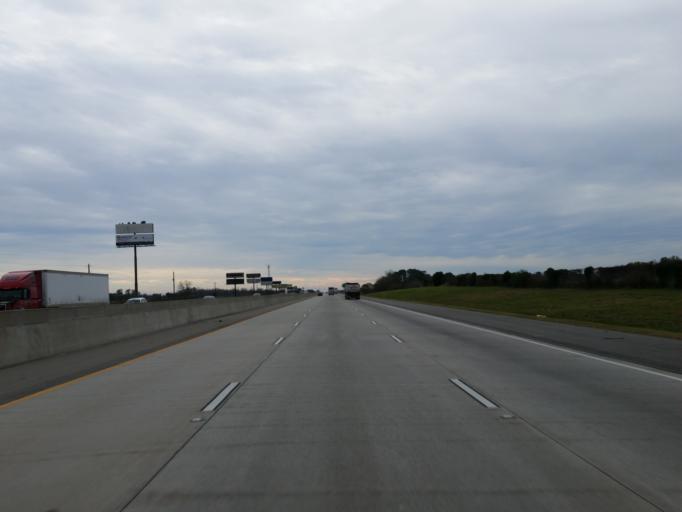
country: US
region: Georgia
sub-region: Tift County
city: Unionville
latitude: 31.3858
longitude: -83.4972
